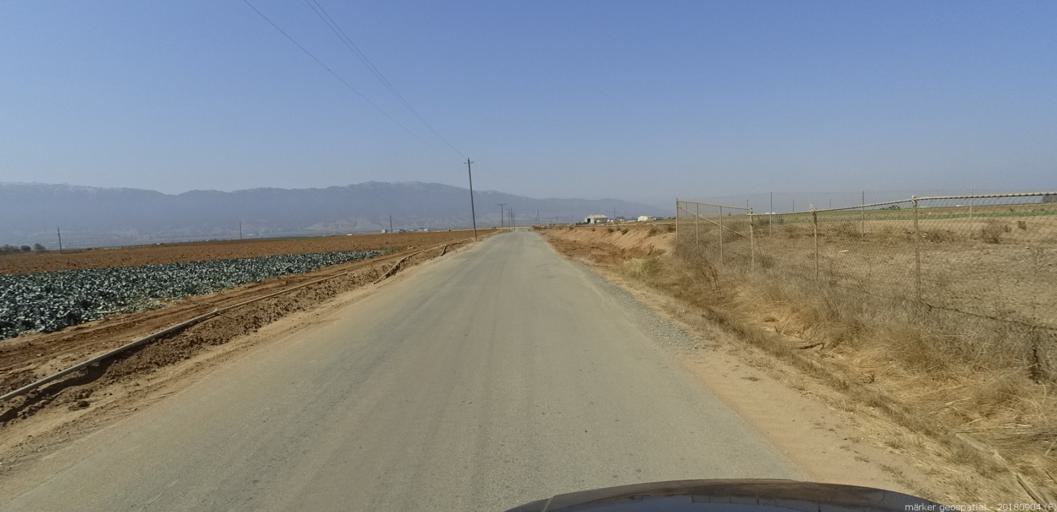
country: US
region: California
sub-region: Monterey County
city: Chualar
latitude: 36.5570
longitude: -121.4739
